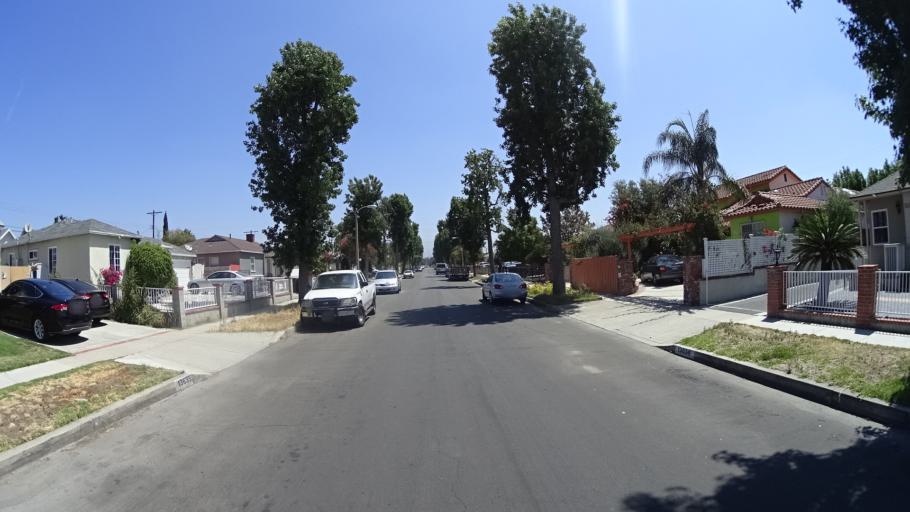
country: US
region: California
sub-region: Los Angeles County
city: Van Nuys
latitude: 34.2304
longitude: -118.4292
